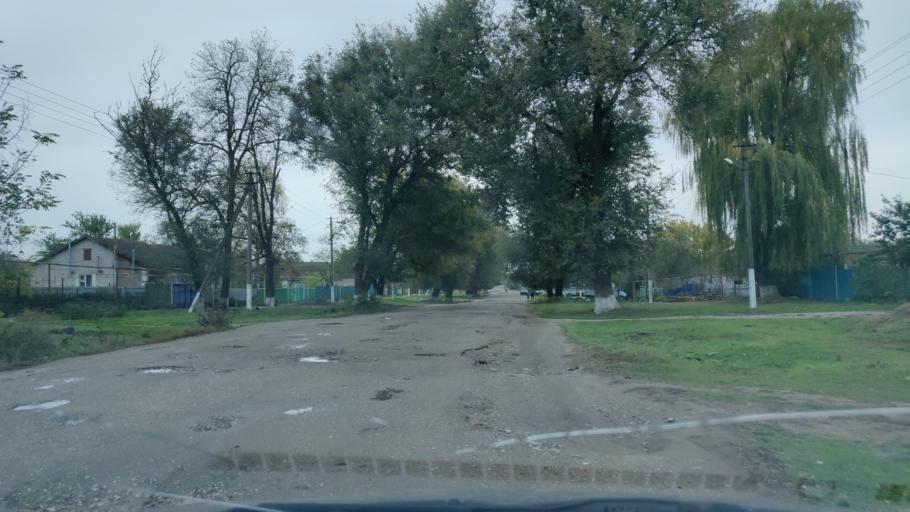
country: RU
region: Stavropol'skiy
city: Irgakly
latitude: 44.2411
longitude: 44.7222
